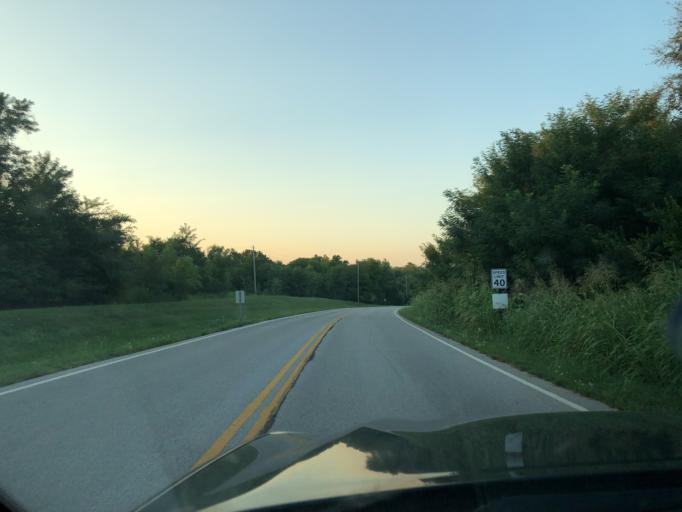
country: US
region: Kansas
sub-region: Leavenworth County
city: Leavenworth
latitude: 39.3315
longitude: -94.9166
